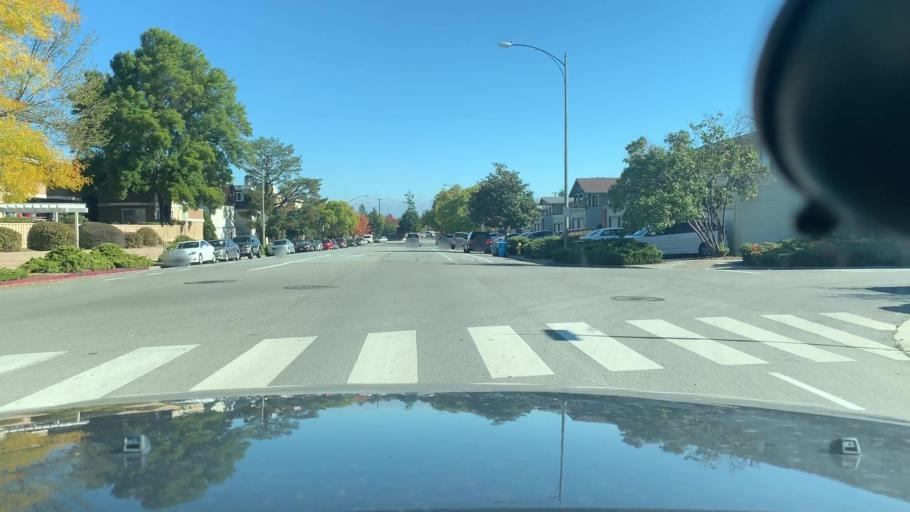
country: US
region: California
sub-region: Santa Clara County
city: Cupertino
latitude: 37.3006
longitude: -122.0354
